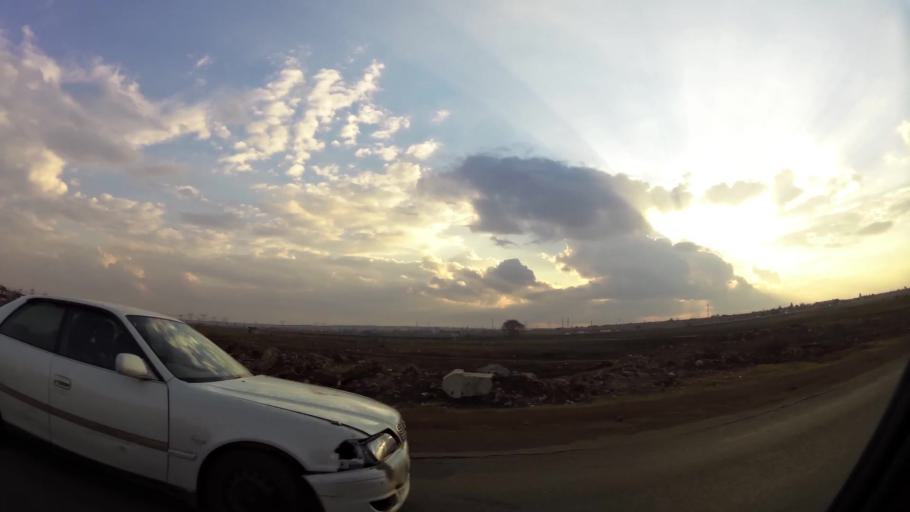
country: ZA
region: Gauteng
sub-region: City of Johannesburg Metropolitan Municipality
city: Orange Farm
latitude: -26.5449
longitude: 27.8332
